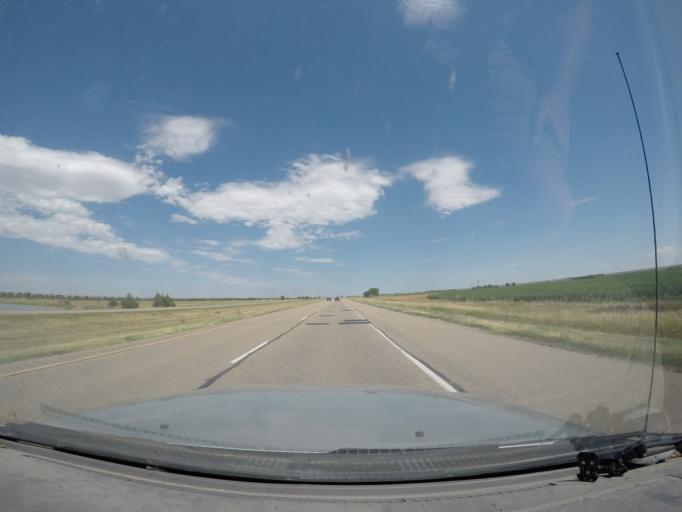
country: US
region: Colorado
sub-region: Sedgwick County
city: Julesburg
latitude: 41.0377
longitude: -102.1255
